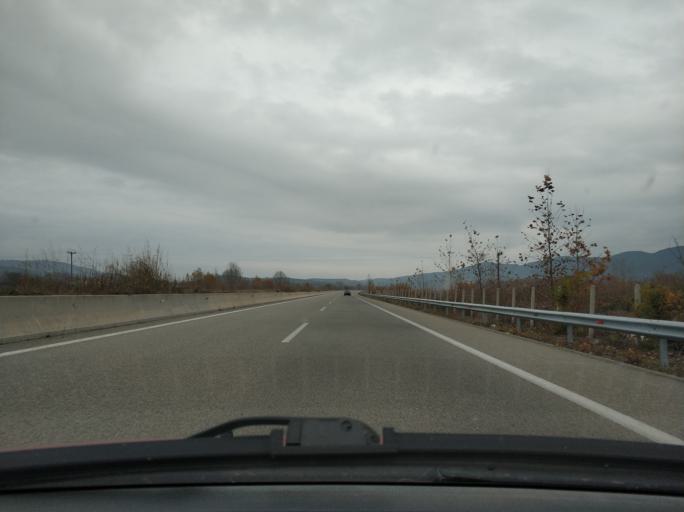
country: GR
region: East Macedonia and Thrace
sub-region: Nomos Kavalas
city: Eleftheres
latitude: 40.8733
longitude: 24.2050
